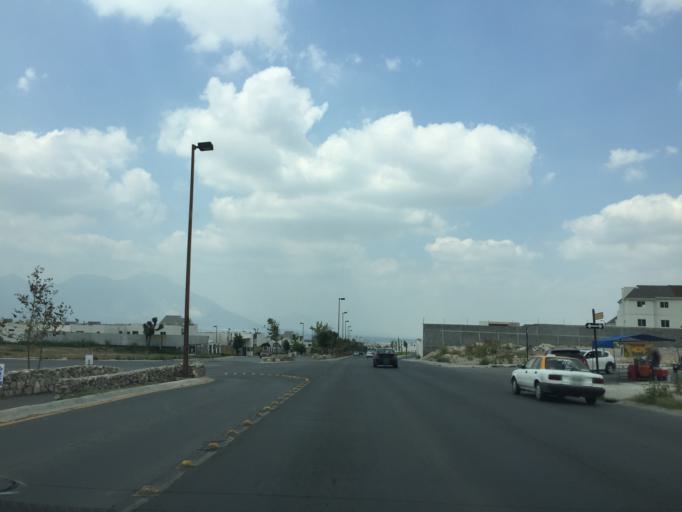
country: MX
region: Nuevo Leon
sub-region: Garcia
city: Mitras Poniente
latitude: 25.7480
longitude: -100.4188
